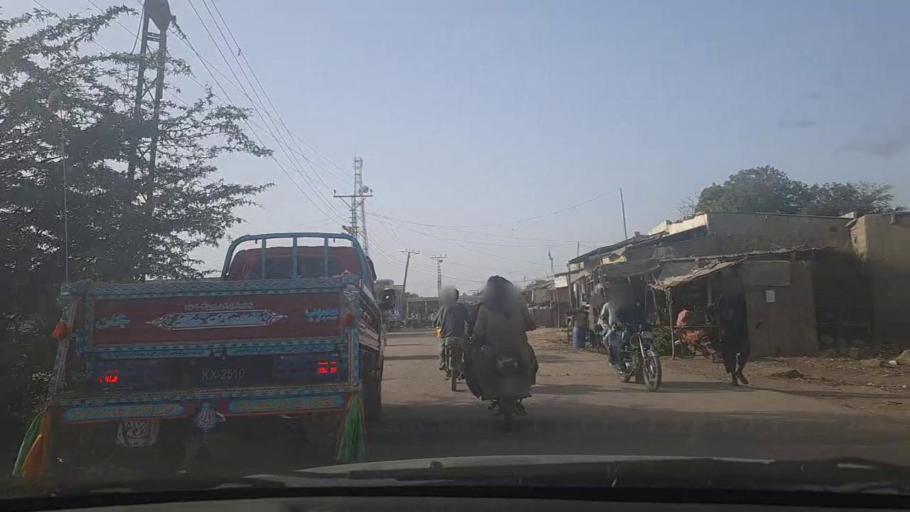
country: PK
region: Sindh
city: Keti Bandar
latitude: 24.3039
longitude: 67.6048
